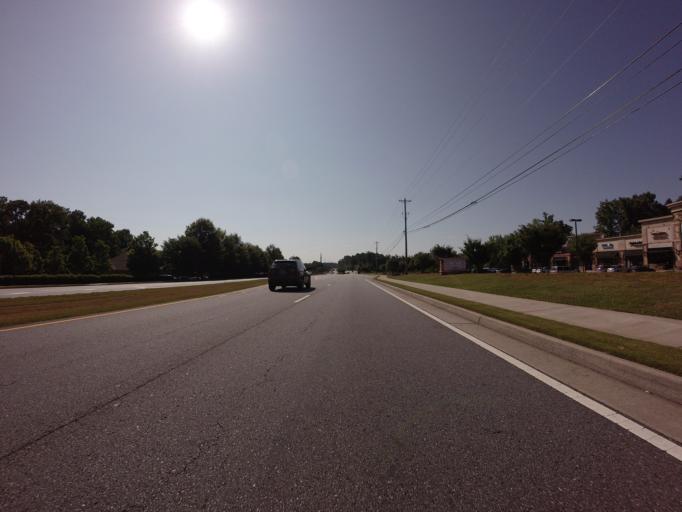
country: US
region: Georgia
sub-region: Fulton County
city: Johns Creek
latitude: 34.0619
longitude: -84.1581
